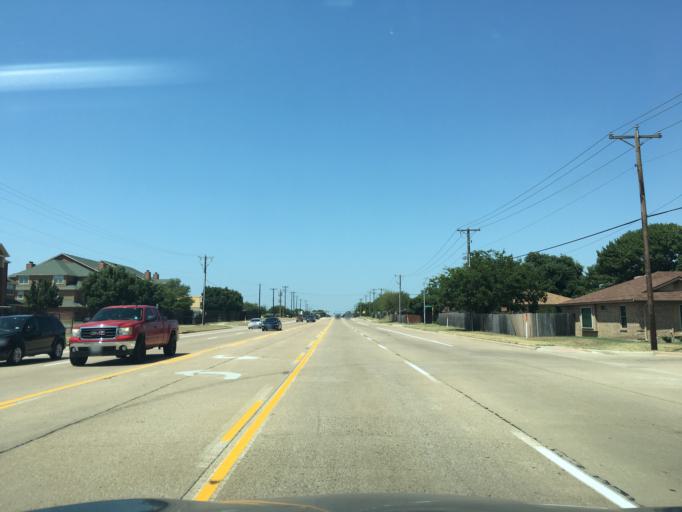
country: US
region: Texas
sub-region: Tarrant County
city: Edgecliff Village
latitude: 32.6303
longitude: -97.3486
